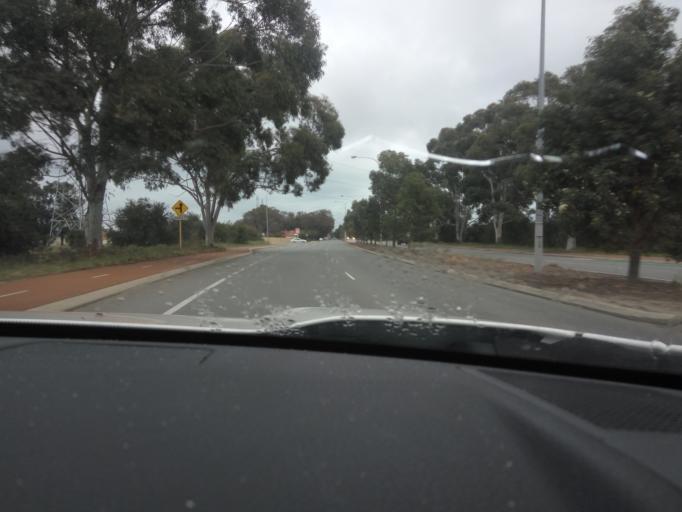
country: AU
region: Western Australia
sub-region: City of Cockburn
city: City of Cockburn
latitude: -32.1108
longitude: 115.8479
